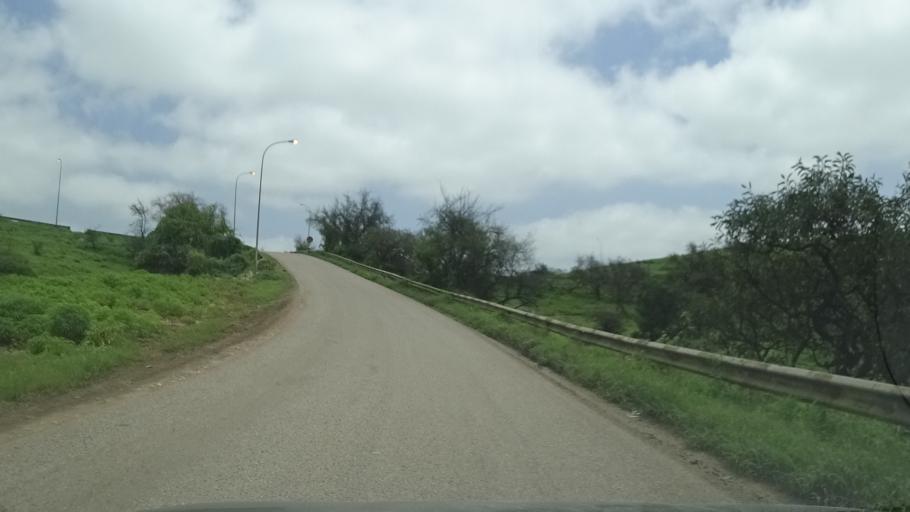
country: OM
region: Zufar
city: Salalah
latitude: 17.1915
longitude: 54.1642
